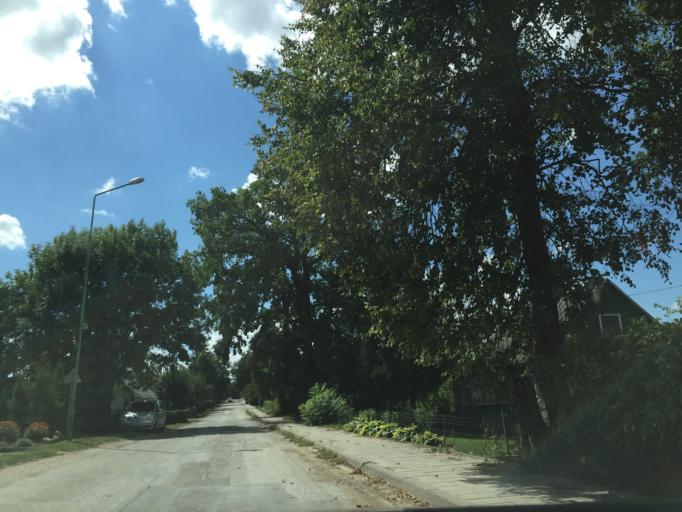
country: LV
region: Rundales
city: Pilsrundale
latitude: 56.2757
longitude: 24.0006
